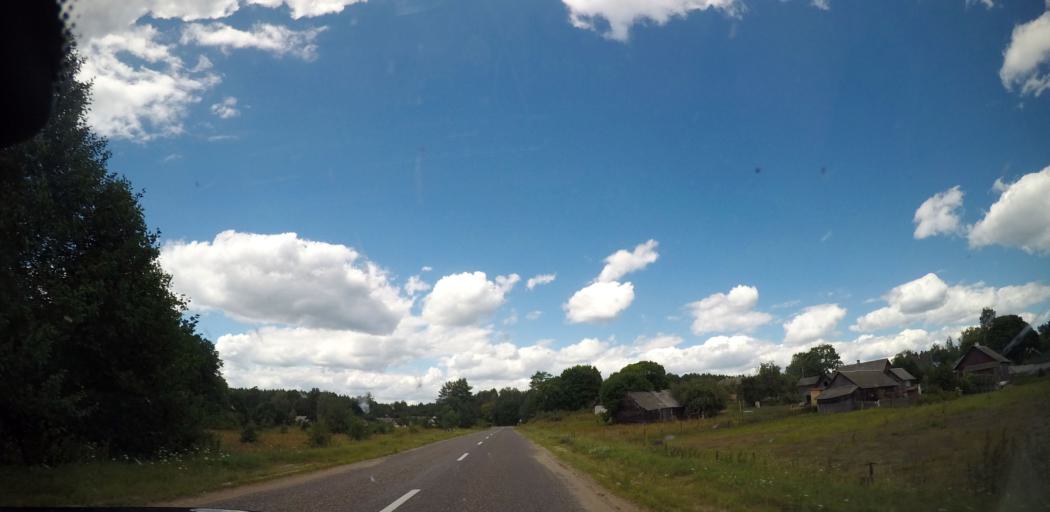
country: BY
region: Grodnenskaya
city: Skidal'
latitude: 53.8212
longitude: 24.2426
